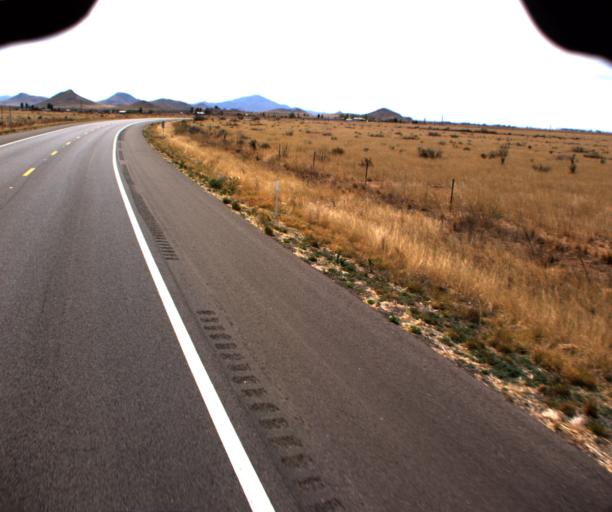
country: US
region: Arizona
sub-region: Cochise County
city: Willcox
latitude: 31.8959
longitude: -109.6991
